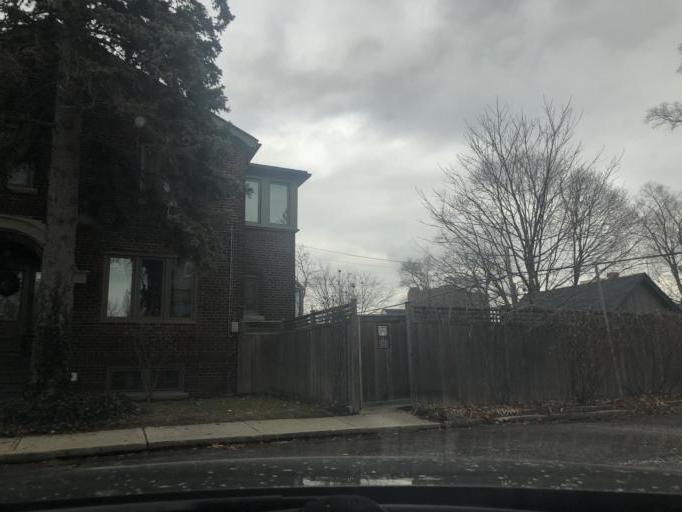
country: CA
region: Ontario
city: Toronto
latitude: 43.6788
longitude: -79.3353
